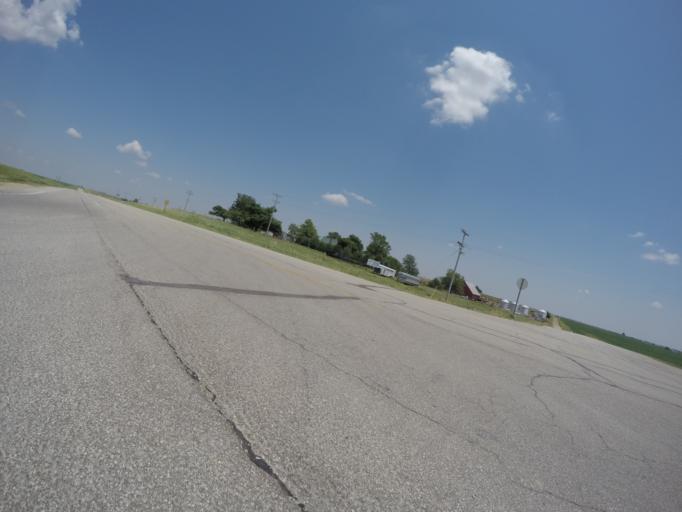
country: US
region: Kansas
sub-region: Doniphan County
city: Troy
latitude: 39.7401
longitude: -95.1439
